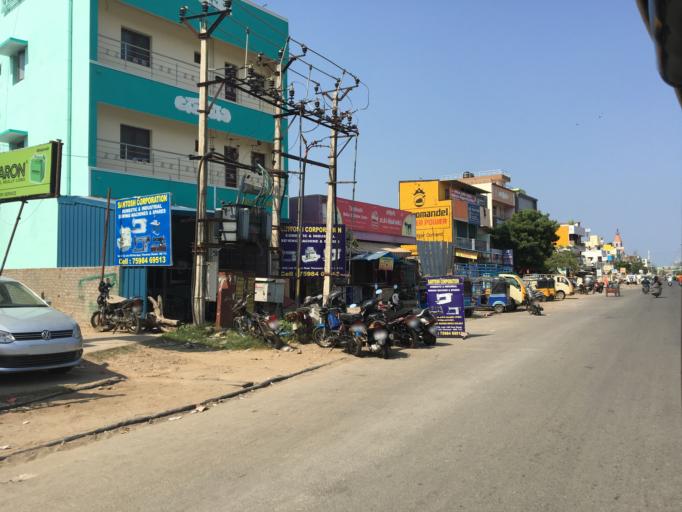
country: IN
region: Tamil Nadu
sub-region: Kancheepuram
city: Perungudi
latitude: 12.9812
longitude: 80.2357
